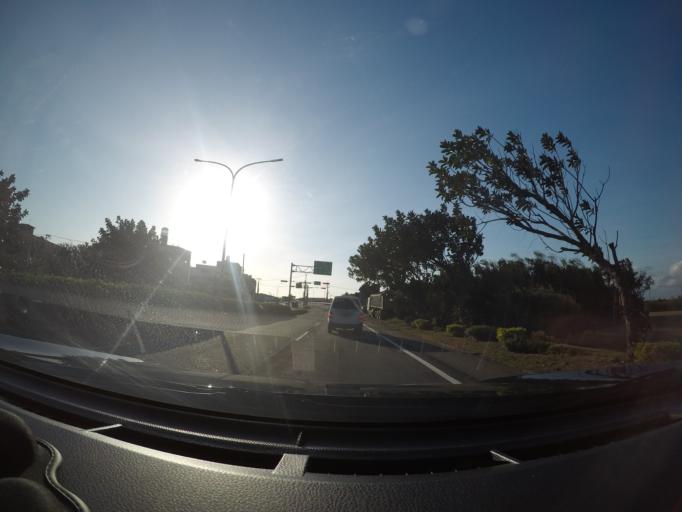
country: TW
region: Taiwan
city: Taoyuan City
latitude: 25.0798
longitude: 121.2115
